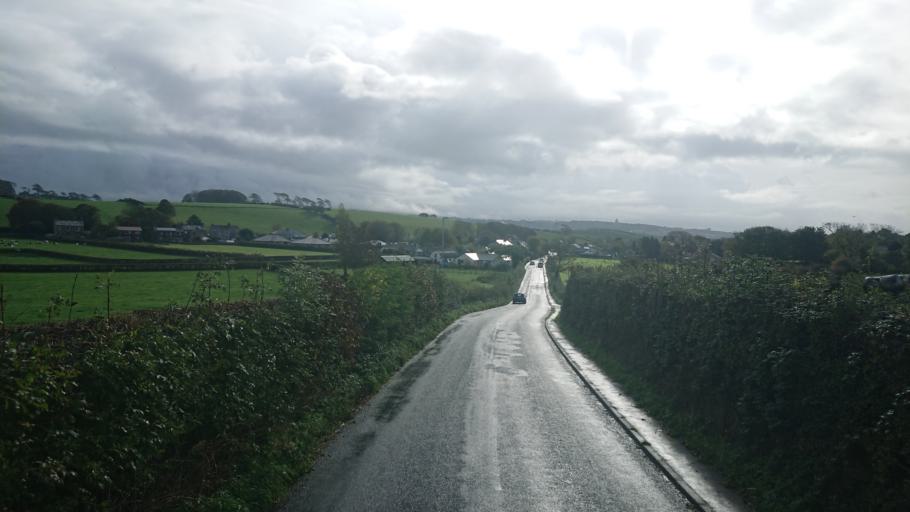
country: GB
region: England
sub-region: Lancashire
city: Bolton le Sands
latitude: 54.0817
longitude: -2.8059
